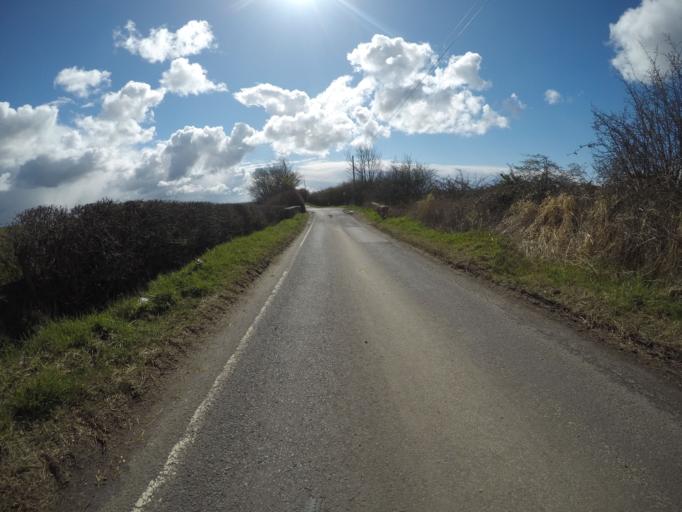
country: GB
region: Scotland
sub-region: North Ayrshire
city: Kilwinning
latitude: 55.6703
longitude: -4.7209
